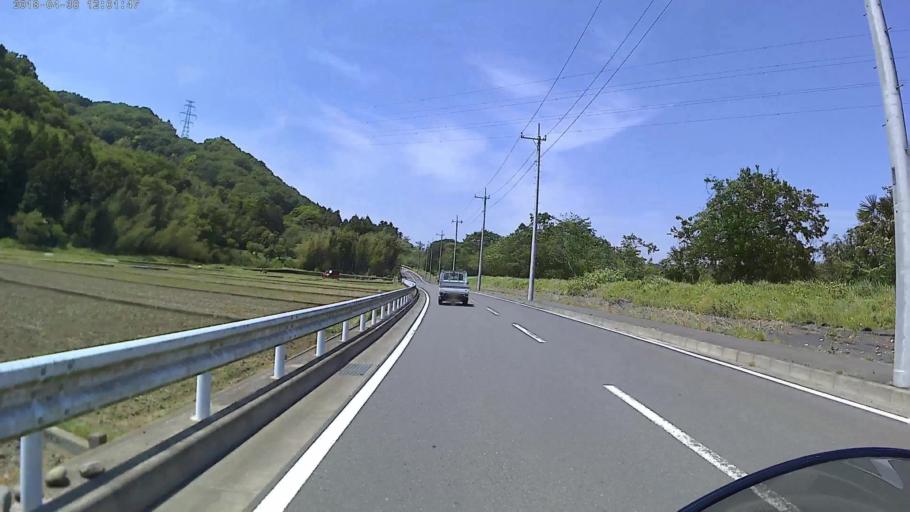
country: JP
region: Kanagawa
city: Zama
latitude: 35.5197
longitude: 139.3235
